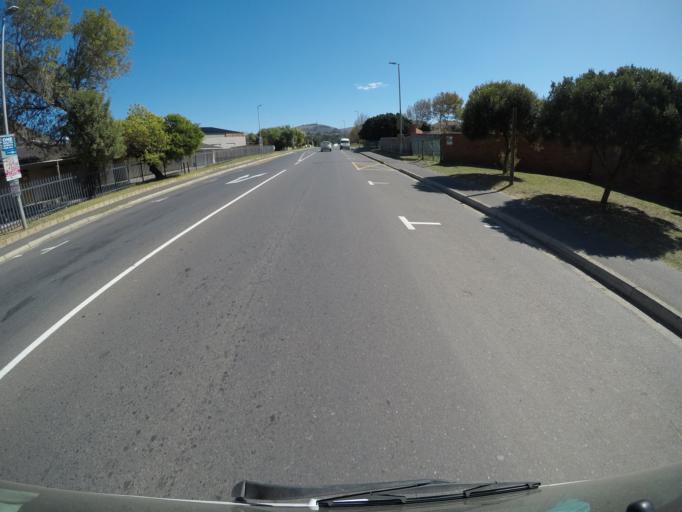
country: ZA
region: Western Cape
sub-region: City of Cape Town
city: Kraaifontein
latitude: -33.8299
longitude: 18.6430
